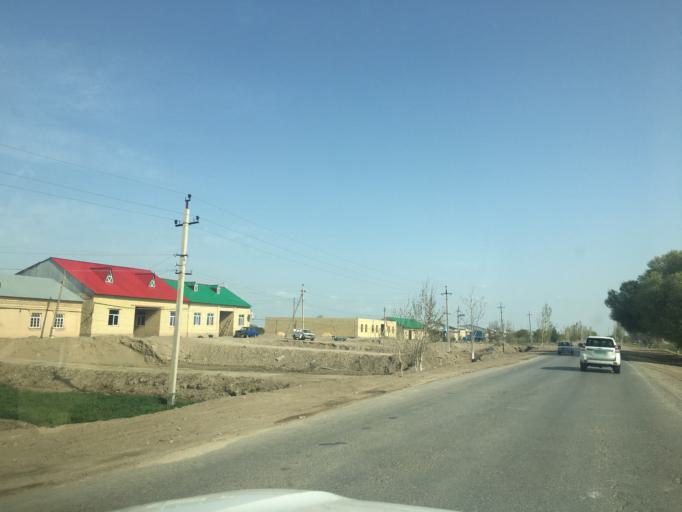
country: TM
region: Lebap
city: Farap
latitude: 39.2033
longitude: 63.5610
